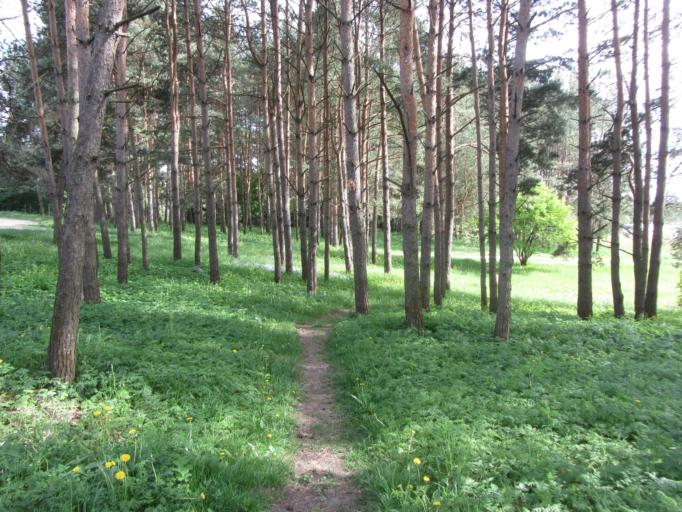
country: LT
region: Utenos apskritis
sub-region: Utena
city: Utena
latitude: 55.4944
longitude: 25.5913
